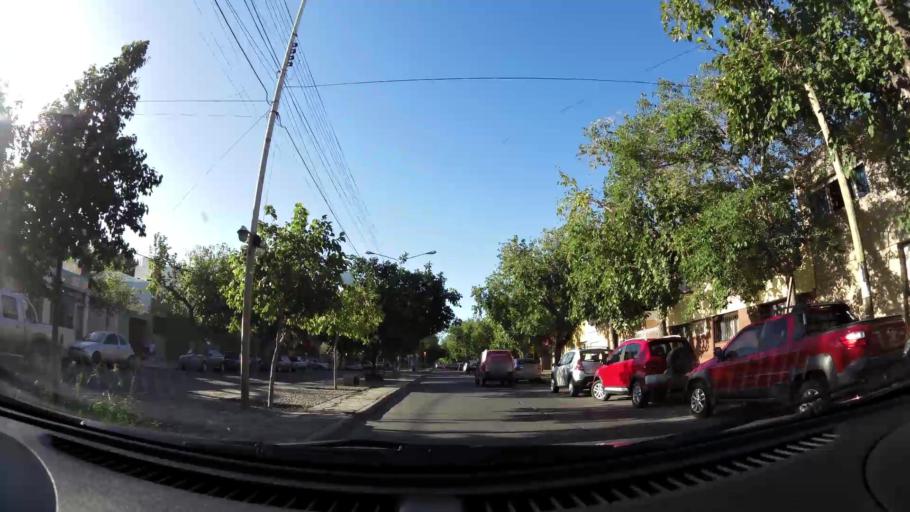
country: AR
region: San Juan
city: San Juan
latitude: -31.5416
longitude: -68.5210
